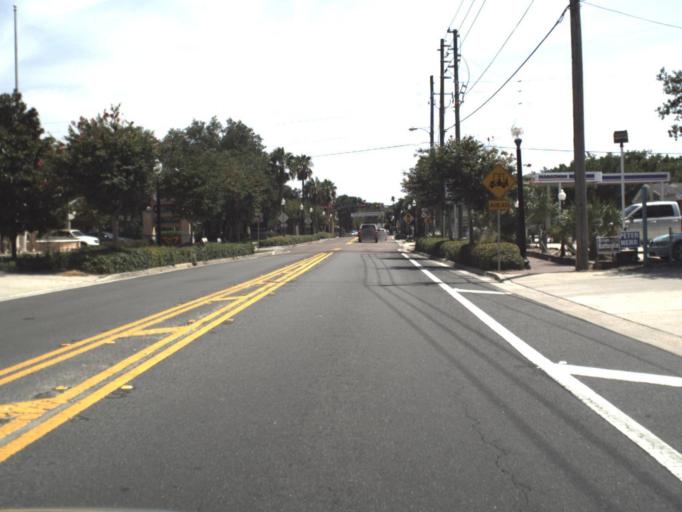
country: US
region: Florida
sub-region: Pinellas County
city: Dunedin
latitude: 28.0140
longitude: -82.7898
